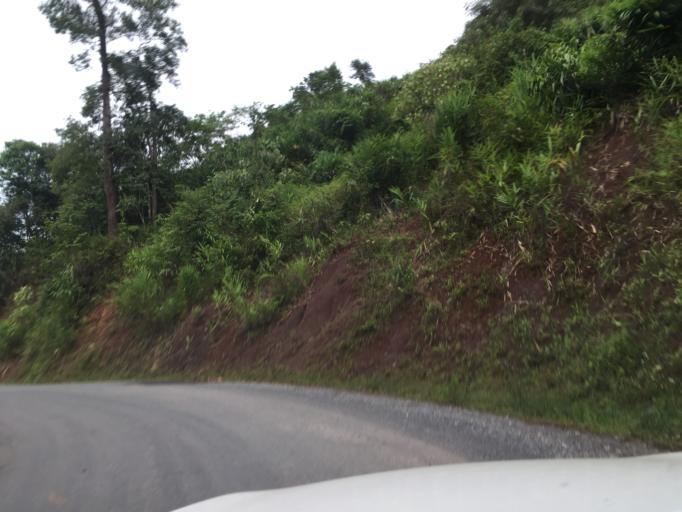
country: LA
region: Phongsali
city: Phongsali
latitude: 21.3420
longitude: 102.0500
